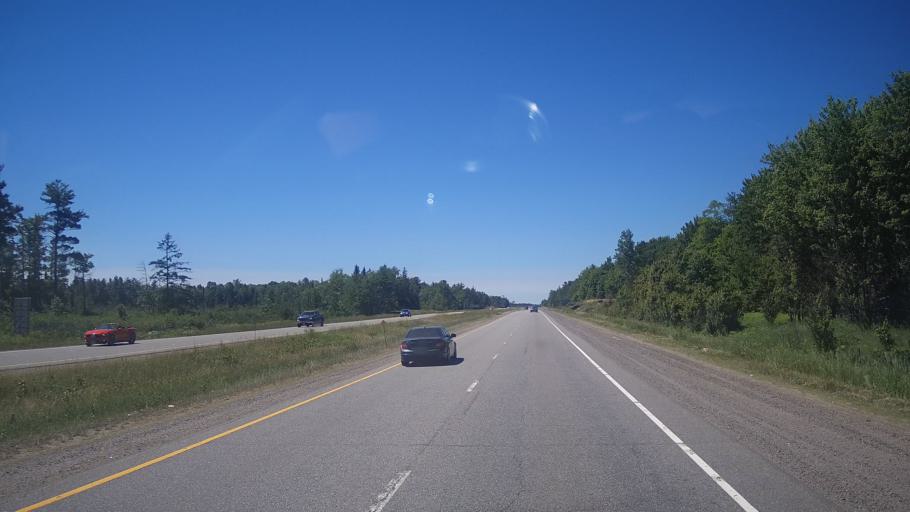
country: CA
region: Ontario
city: Bracebridge
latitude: 44.9768
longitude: -79.3171
